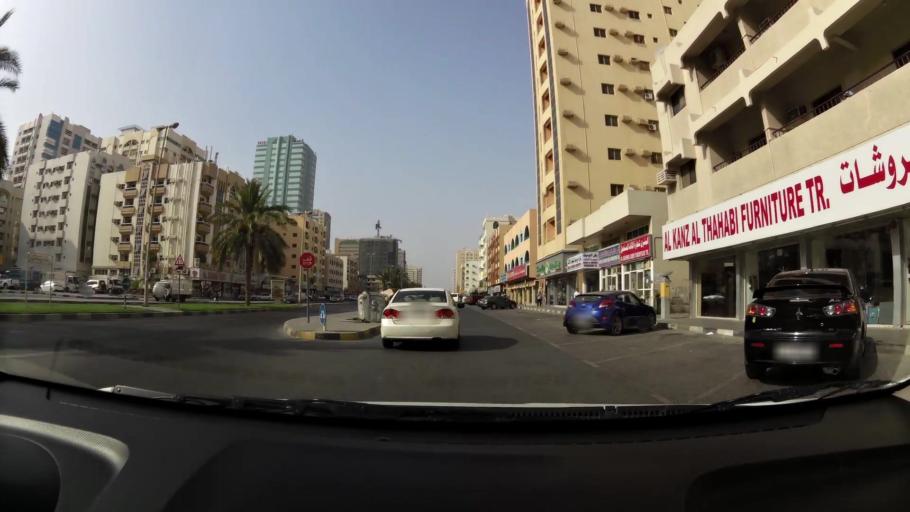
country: AE
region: Ash Shariqah
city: Sharjah
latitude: 25.3392
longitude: 55.3934
